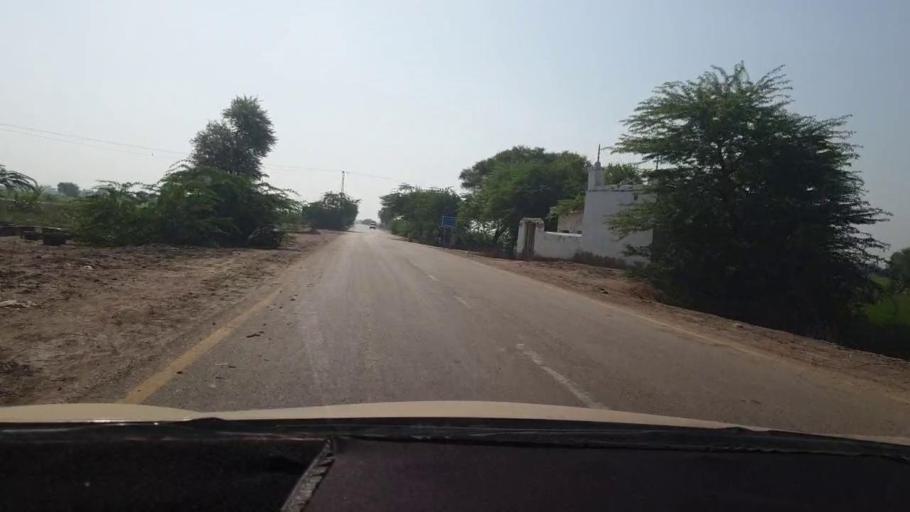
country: PK
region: Sindh
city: Miro Khan
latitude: 27.7218
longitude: 68.1425
